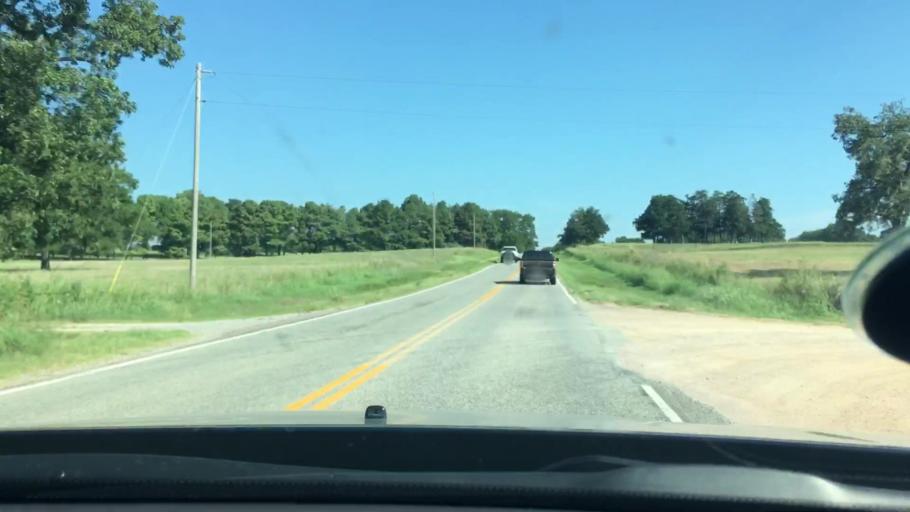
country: US
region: Oklahoma
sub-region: Johnston County
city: Tishomingo
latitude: 34.2593
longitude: -96.5487
